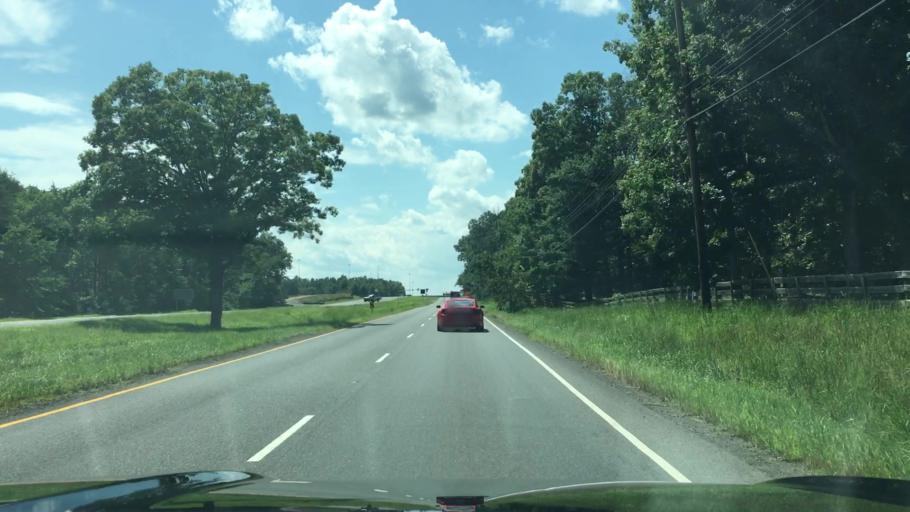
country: US
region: Virginia
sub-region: Prince William County
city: Gainesville
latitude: 38.8028
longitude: -77.5872
